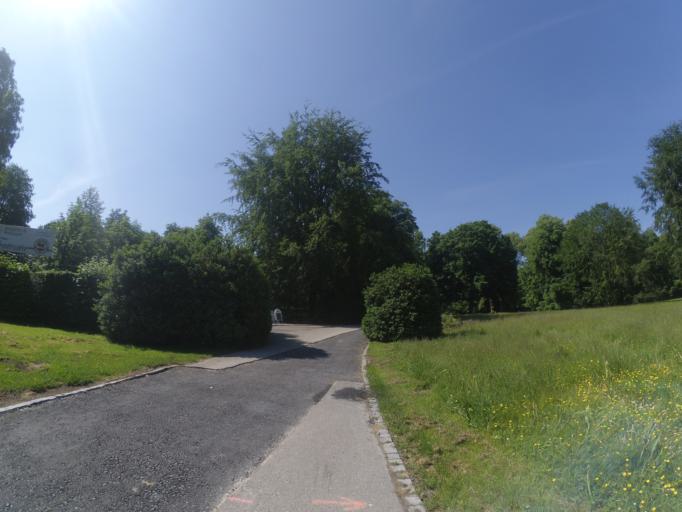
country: DE
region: Bavaria
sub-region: Swabia
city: Neu-Ulm
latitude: 48.4082
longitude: 10.0138
